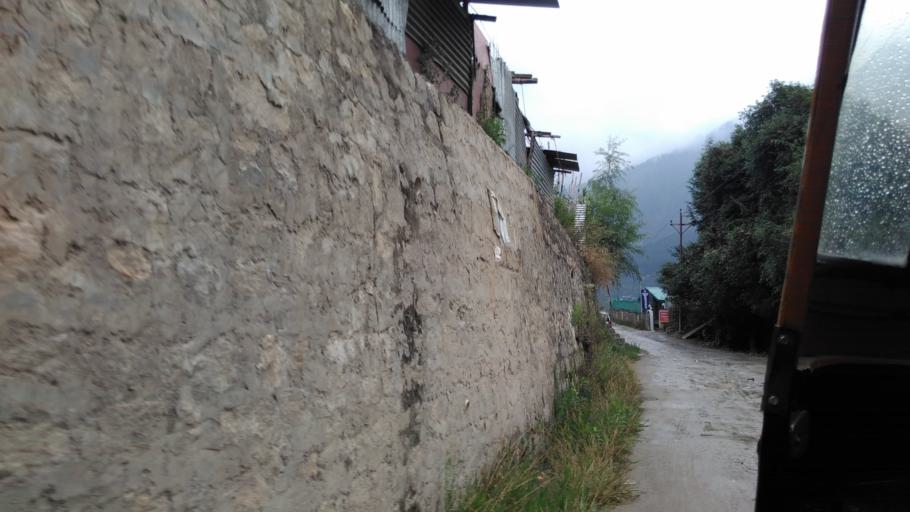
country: IN
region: Himachal Pradesh
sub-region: Kulu
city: Manali
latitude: 32.2255
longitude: 77.1850
